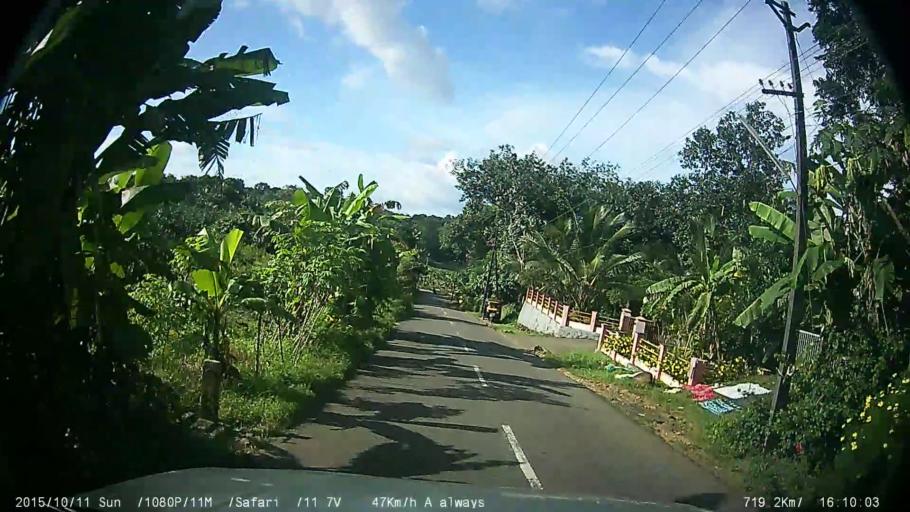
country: IN
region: Kerala
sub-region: Kottayam
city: Palackattumala
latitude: 9.7002
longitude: 76.6101
